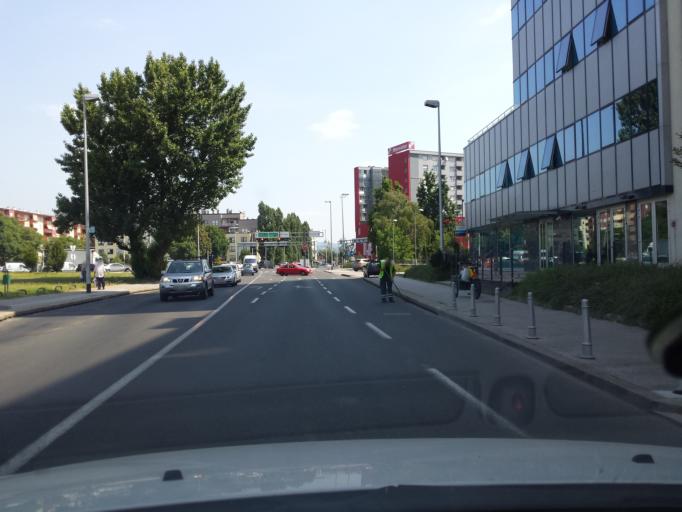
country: HR
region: Grad Zagreb
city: Jankomir
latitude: 45.7953
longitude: 15.9080
